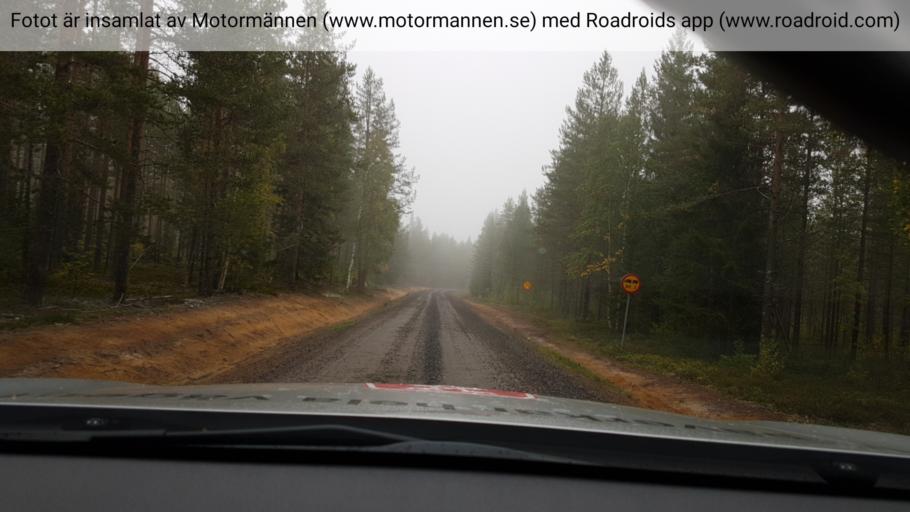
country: SE
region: Vaesterbotten
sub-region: Umea Kommun
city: Ersmark
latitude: 64.1476
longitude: 20.3750
